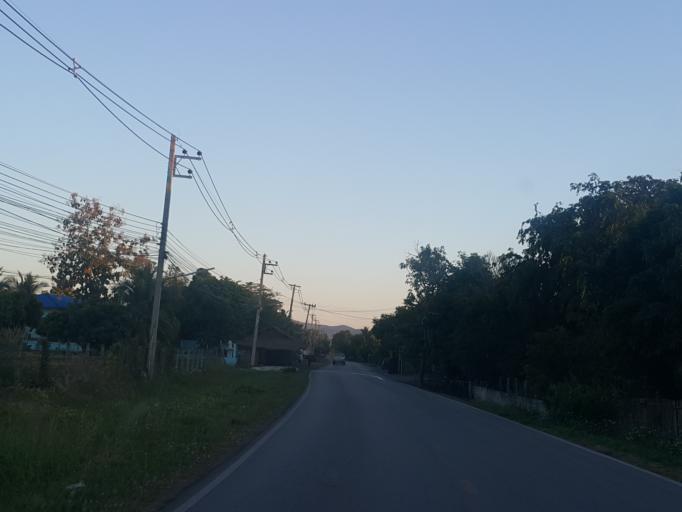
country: TH
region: Chiang Mai
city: San Kamphaeng
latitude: 18.8389
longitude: 99.1500
